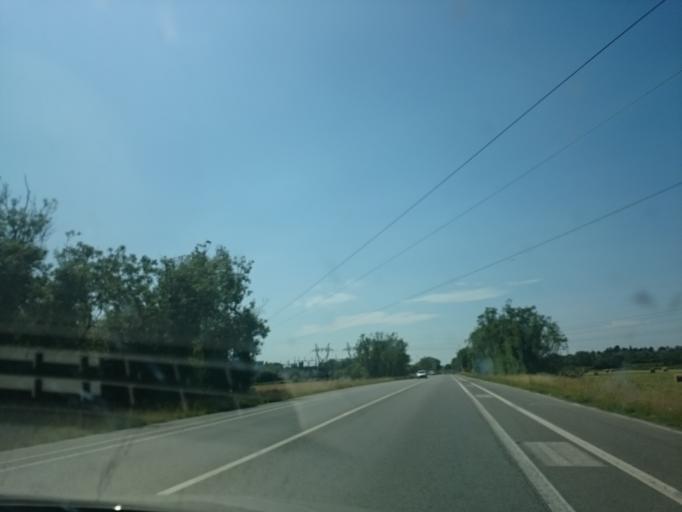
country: FR
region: Pays de la Loire
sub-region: Departement de la Loire-Atlantique
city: Indre
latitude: 47.2058
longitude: -1.6794
